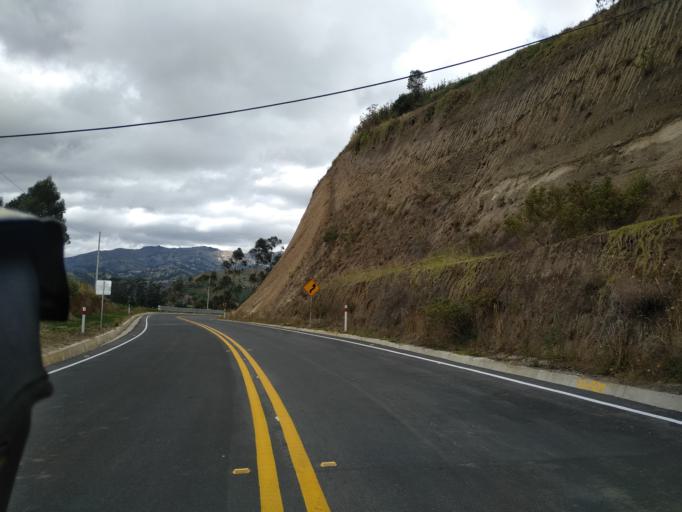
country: EC
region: Cotopaxi
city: Saquisili
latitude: -0.7682
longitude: -78.9088
